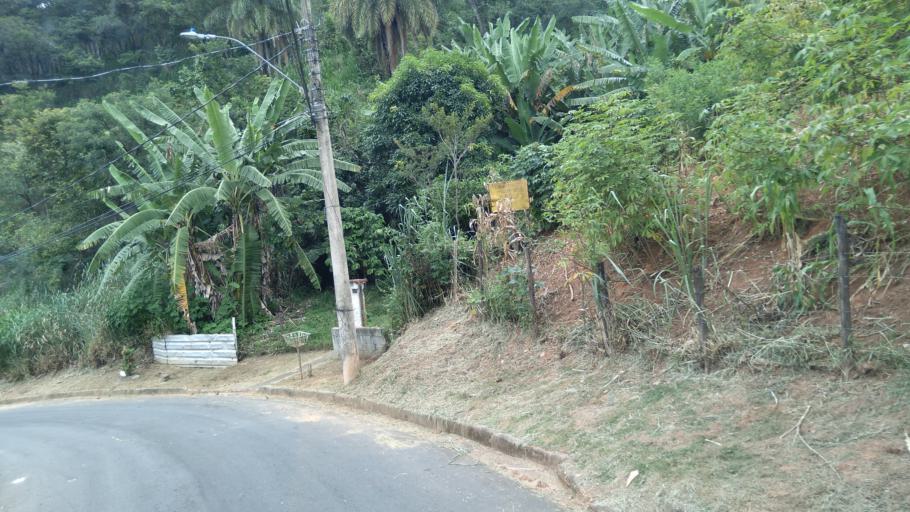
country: BR
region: Minas Gerais
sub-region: Contagem
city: Contagem
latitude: -19.9123
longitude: -44.0067
